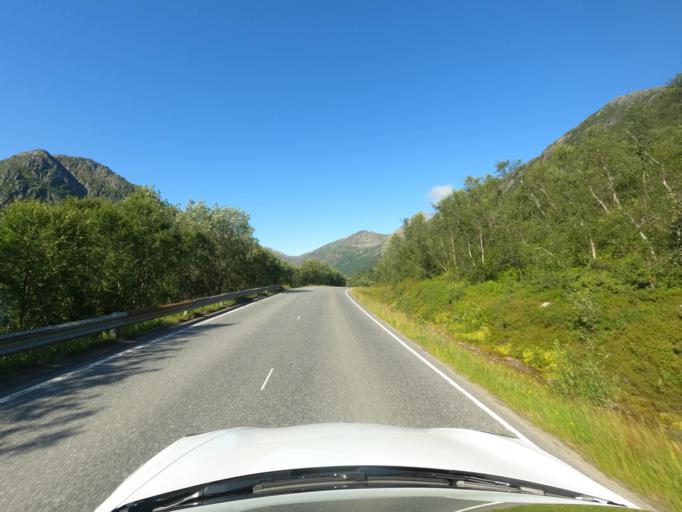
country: NO
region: Nordland
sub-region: Lodingen
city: Lodingen
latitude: 68.5594
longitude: 15.7678
